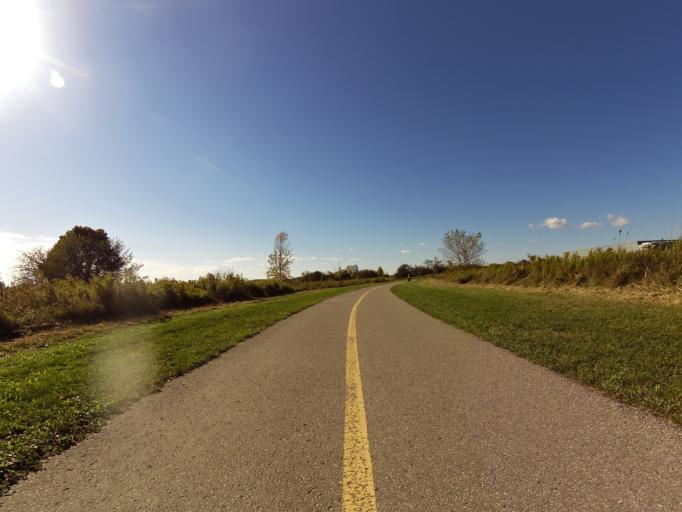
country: CA
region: Ontario
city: Oshawa
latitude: 43.8521
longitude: -78.8773
